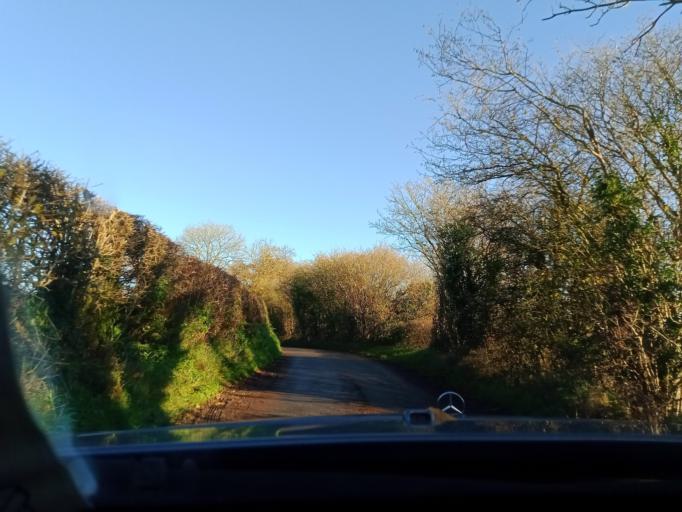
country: IE
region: Leinster
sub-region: Kilkenny
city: Mooncoin
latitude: 52.3360
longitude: -7.2579
